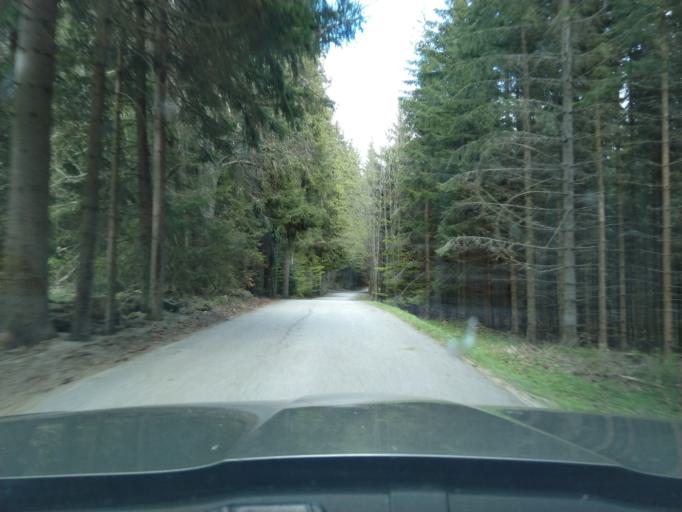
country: CZ
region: Jihocesky
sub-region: Okres Prachatice
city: Borova Lada
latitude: 49.0027
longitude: 13.6981
